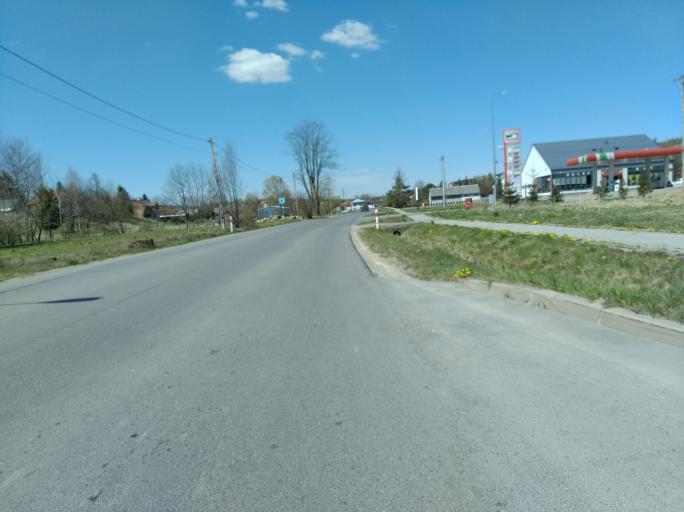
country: PL
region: Subcarpathian Voivodeship
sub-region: Powiat brzozowski
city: Dydnia
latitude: 49.6876
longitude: 22.1681
